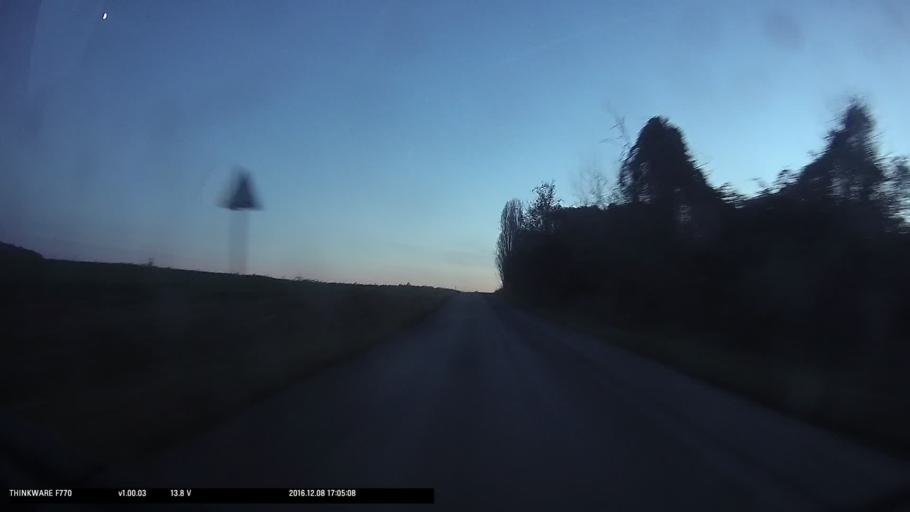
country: FR
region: Ile-de-France
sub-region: Departement du Val-d'Oise
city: Ableiges
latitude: 49.0704
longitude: 2.0049
